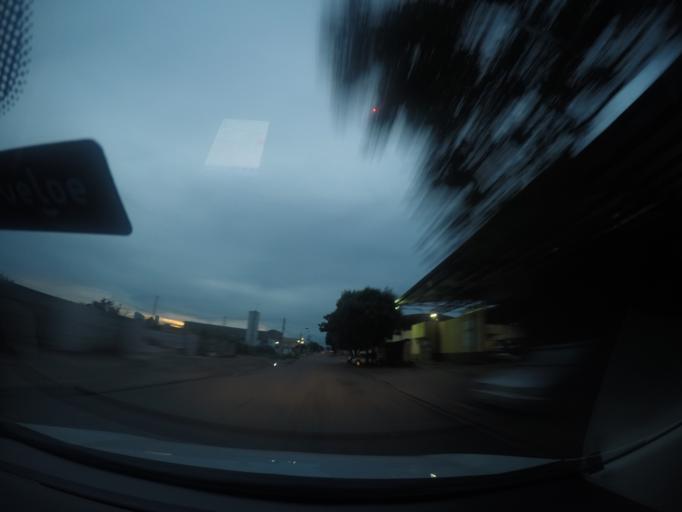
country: BR
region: Goias
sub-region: Goiania
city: Goiania
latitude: -16.6441
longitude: -49.2374
